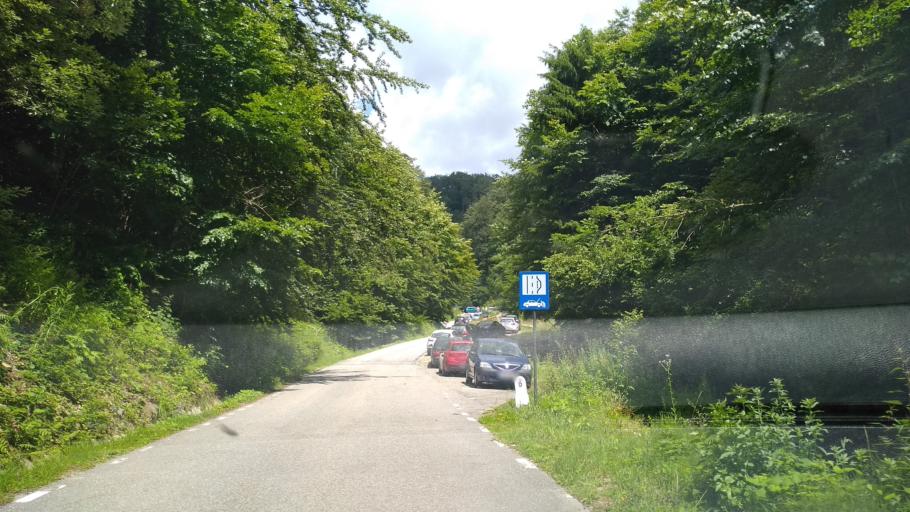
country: RO
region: Hunedoara
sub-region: Comuna Orastioara de Sus
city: Orastioara de Sus
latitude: 45.6238
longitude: 23.3063
